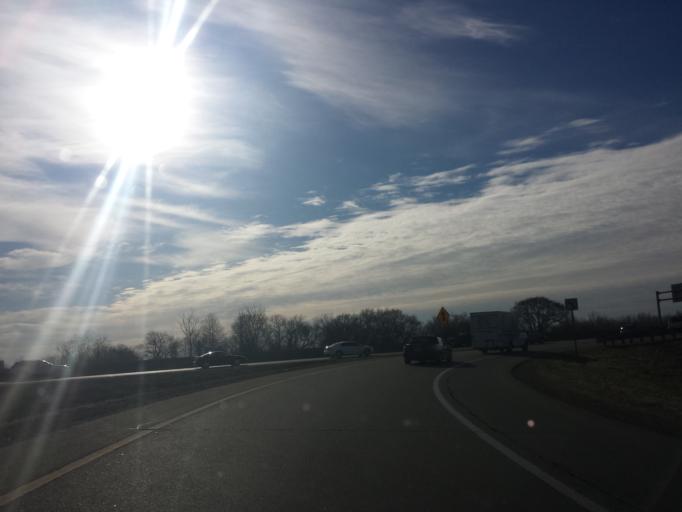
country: US
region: Michigan
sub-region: Oakland County
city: Auburn Hills
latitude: 42.6431
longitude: -83.2393
